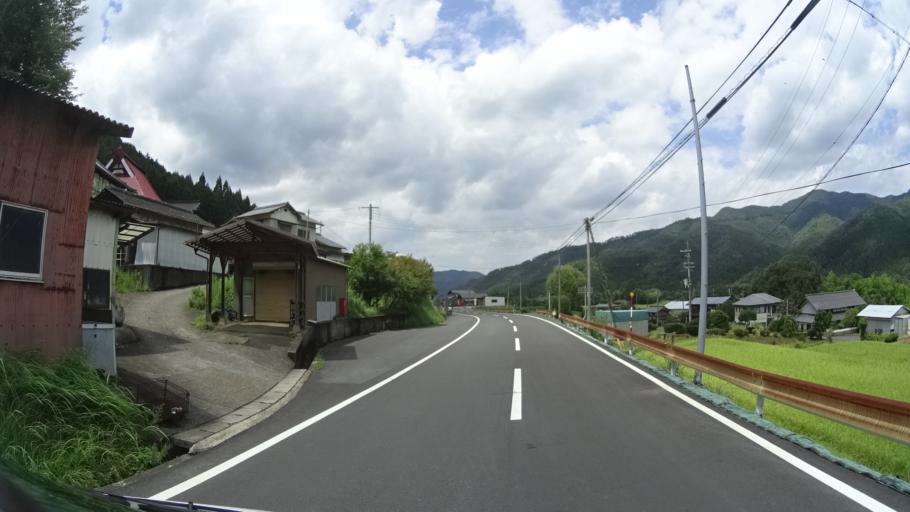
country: JP
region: Kyoto
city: Ayabe
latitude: 35.2716
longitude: 135.3601
